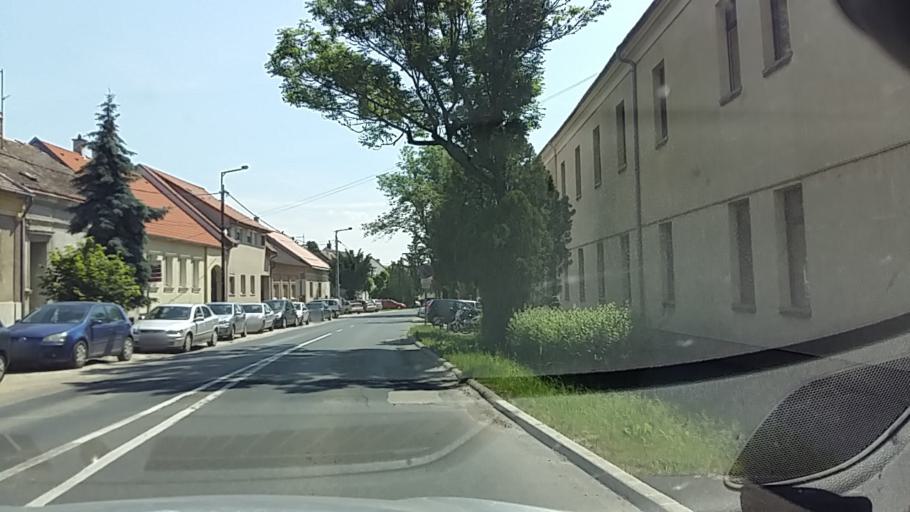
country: HU
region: Gyor-Moson-Sopron
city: Sopron
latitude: 47.6836
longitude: 16.5995
